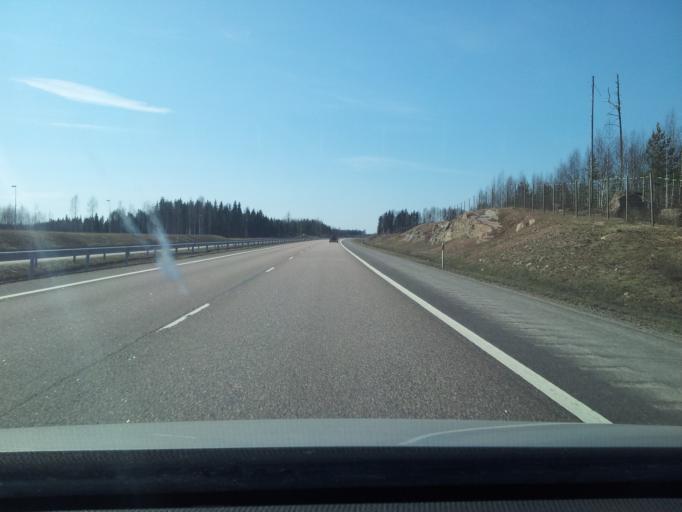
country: FI
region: Kymenlaakso
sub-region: Kotka-Hamina
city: Broby
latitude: 60.4945
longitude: 26.6656
